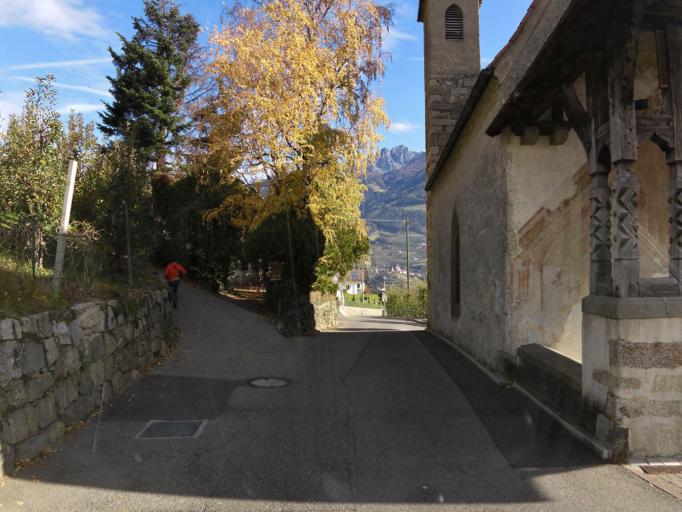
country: IT
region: Trentino-Alto Adige
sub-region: Bolzano
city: Tirolo
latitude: 46.6884
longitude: 11.1597
